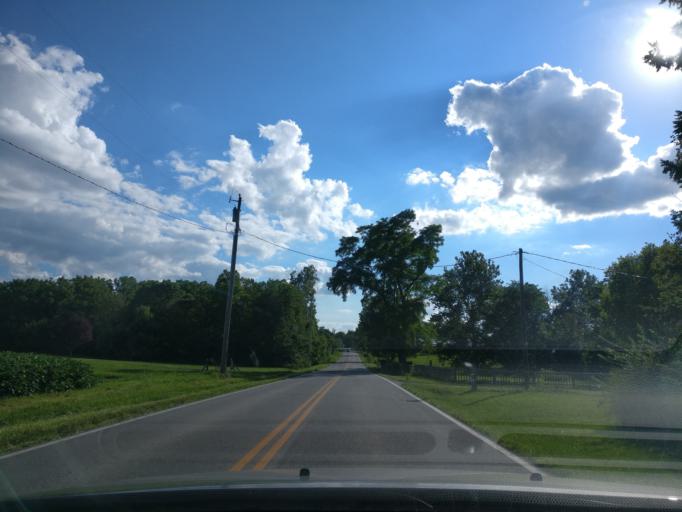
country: US
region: Ohio
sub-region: Clinton County
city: Wilmington
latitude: 39.4674
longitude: -83.8006
